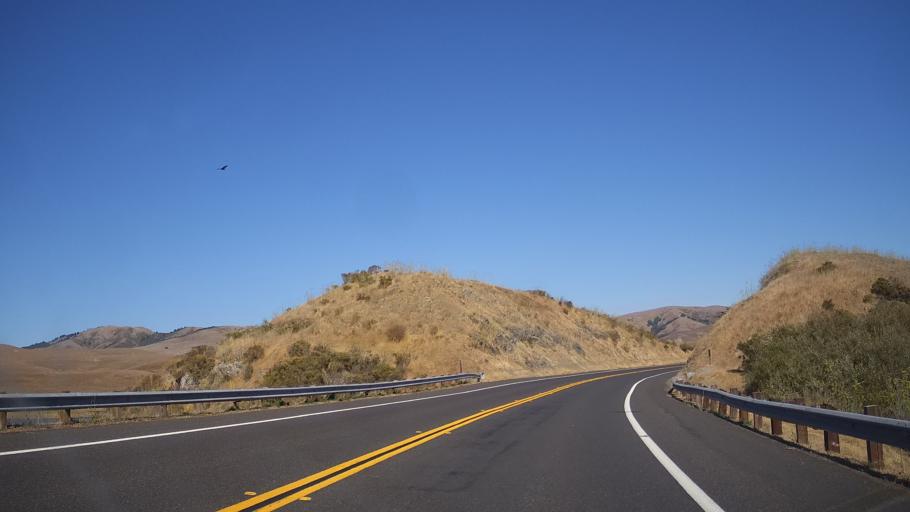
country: US
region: California
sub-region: Marin County
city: Lagunitas-Forest Knolls
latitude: 38.0913
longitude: -122.7512
